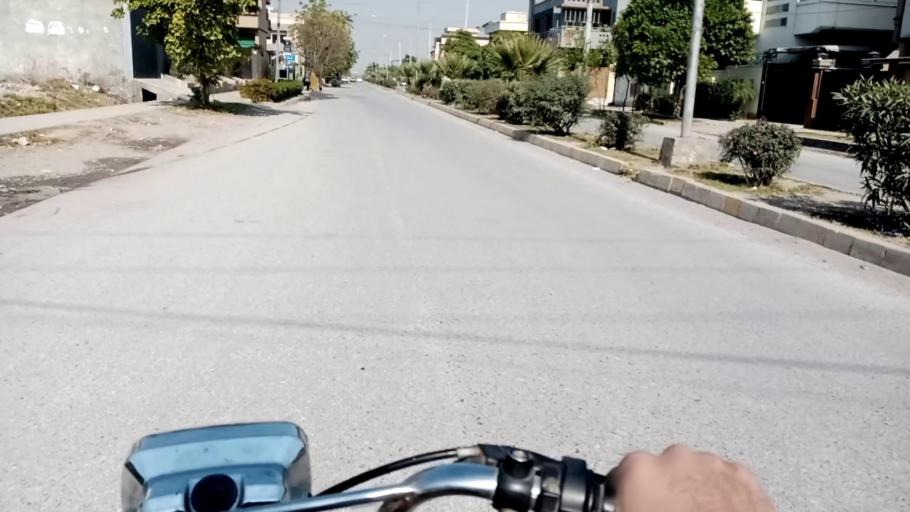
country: PK
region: Khyber Pakhtunkhwa
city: Peshawar
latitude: 33.9591
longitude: 71.4174
